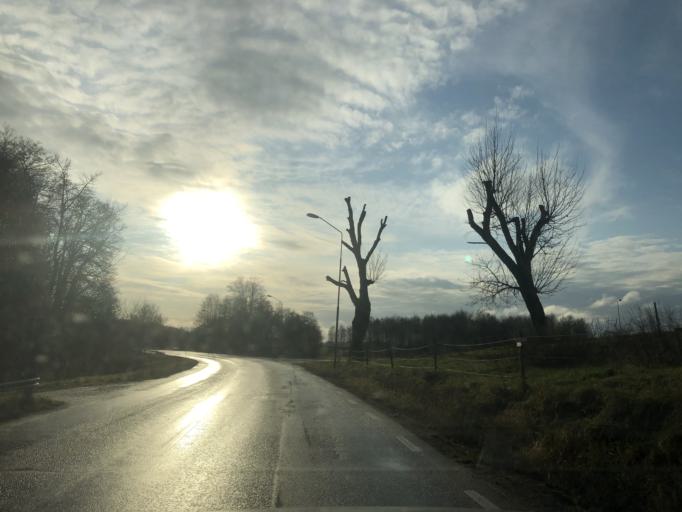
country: SE
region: Vaestra Goetaland
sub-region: Ulricehamns Kommun
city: Ulricehamn
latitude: 57.7440
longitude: 13.4180
